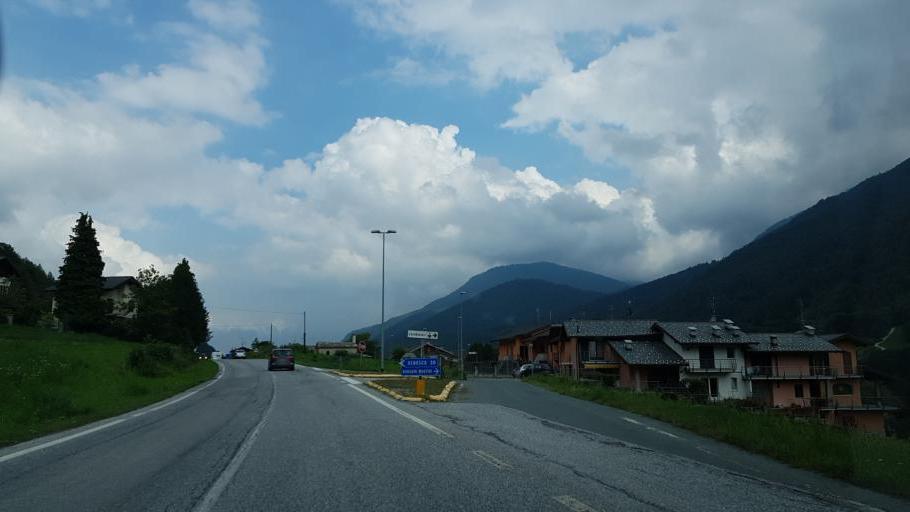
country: IT
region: Piedmont
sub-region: Provincia di Cuneo
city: Sampeyre
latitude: 44.5809
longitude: 7.1766
